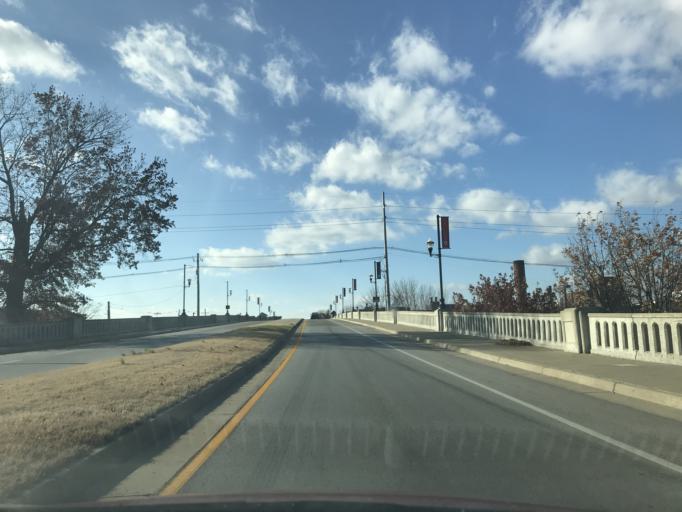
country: US
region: Kentucky
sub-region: Jefferson County
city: Audubon Park
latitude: 38.2131
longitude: -85.7545
